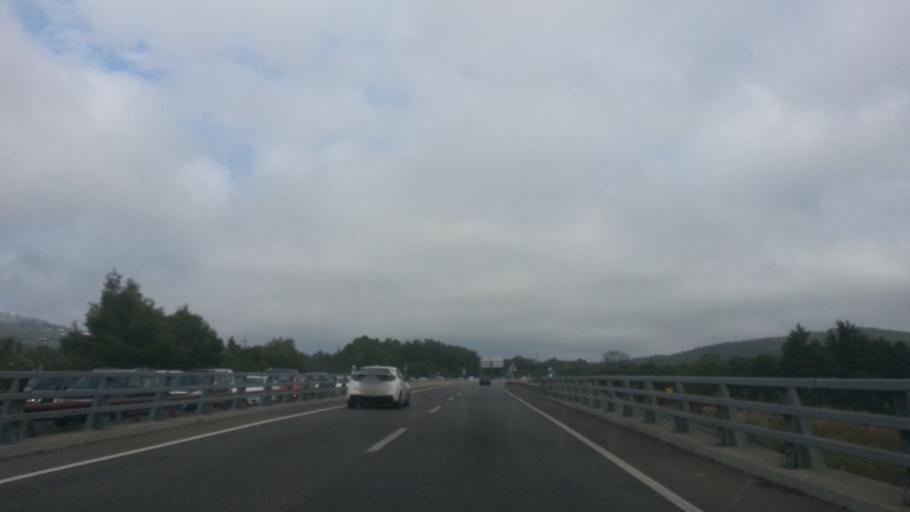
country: ES
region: Catalonia
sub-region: Provincia de Girona
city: Santa Cristina d'Aro
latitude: 41.8086
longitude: 3.0040
